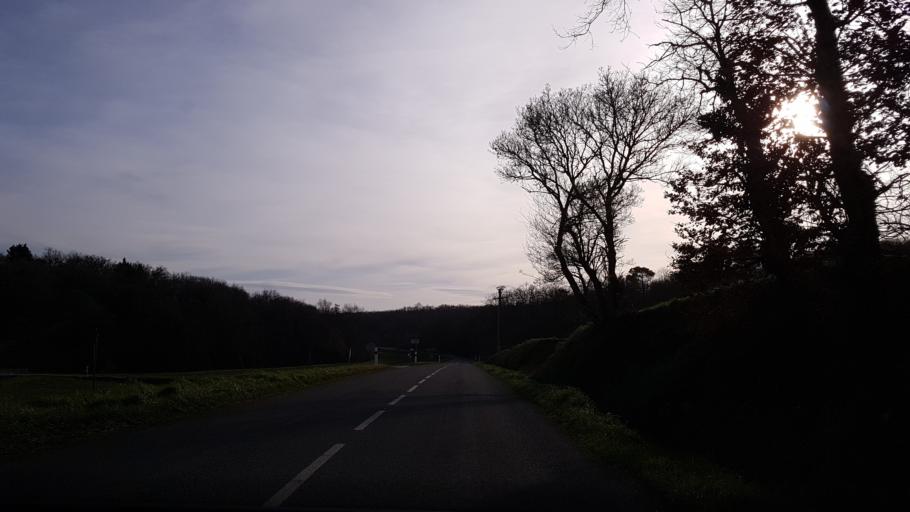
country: FR
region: Languedoc-Roussillon
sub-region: Departement de l'Aude
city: Villeneuve-la-Comptal
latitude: 43.2209
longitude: 1.9159
